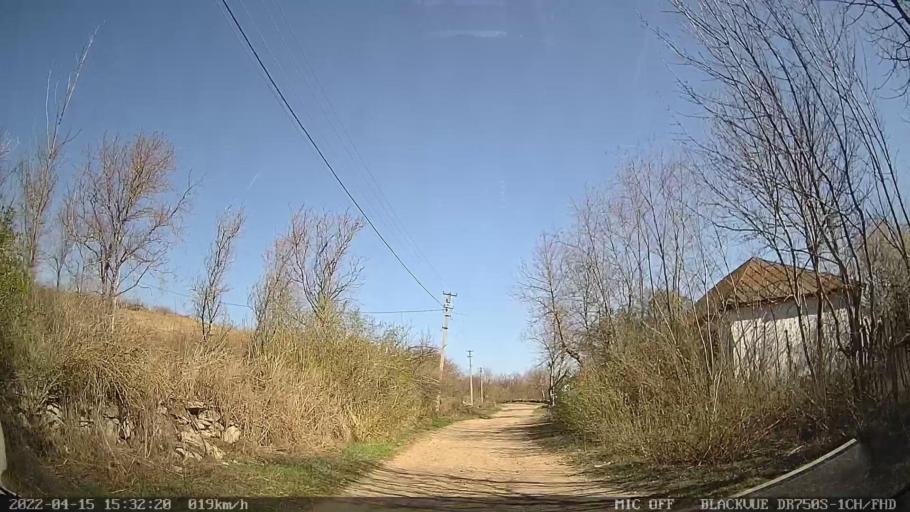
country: MD
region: Raionul Ocnita
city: Otaci
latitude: 48.3511
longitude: 27.9199
